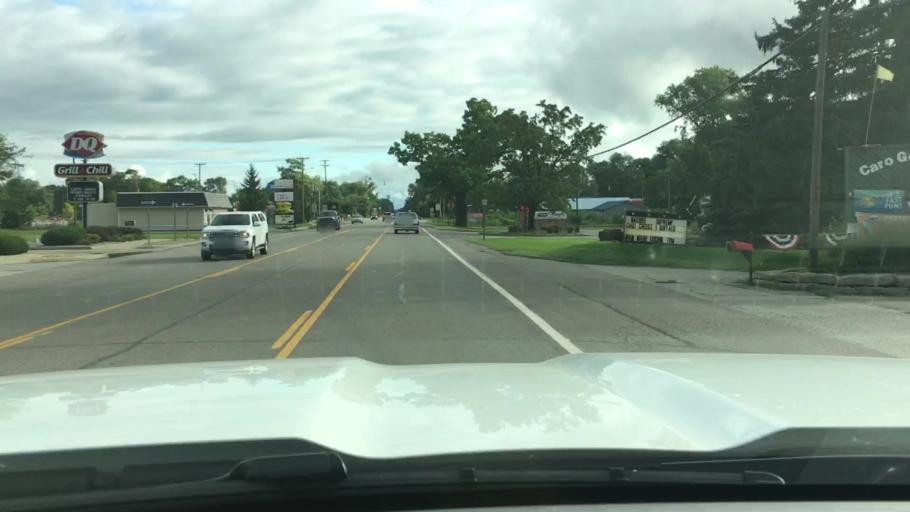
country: US
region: Michigan
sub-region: Tuscola County
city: Caro
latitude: 43.4980
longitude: -83.3844
